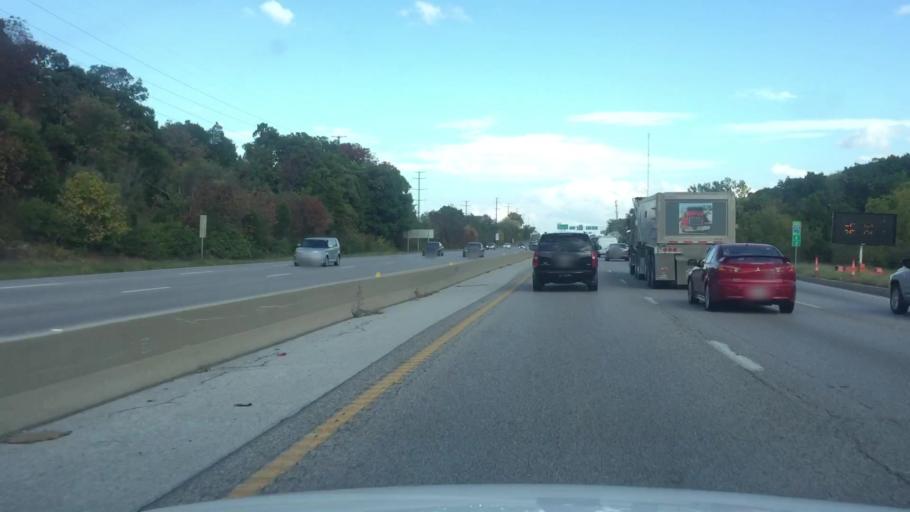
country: US
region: Missouri
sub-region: Jackson County
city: Lees Summit
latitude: 38.9351
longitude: -94.4324
